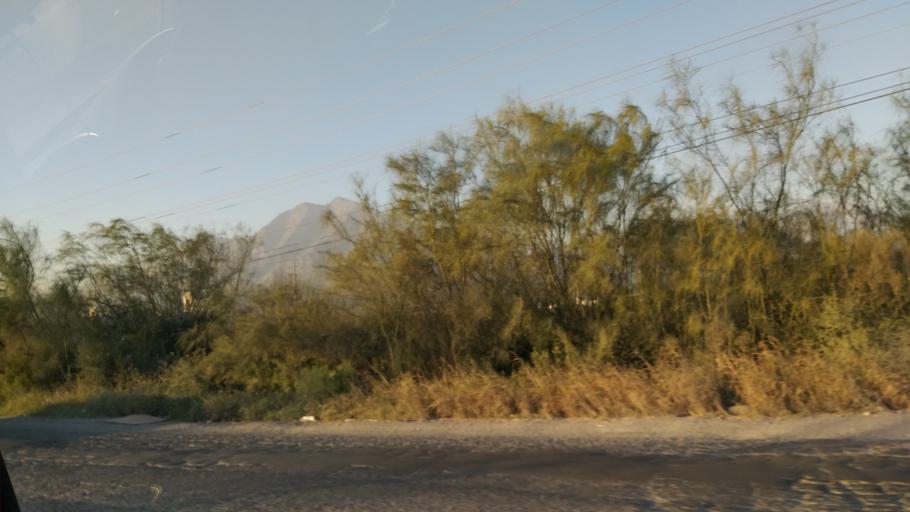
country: MX
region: Nuevo Leon
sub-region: Garcia
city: Parque Industrial Ciudad Mitras
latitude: 25.7784
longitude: -100.4466
